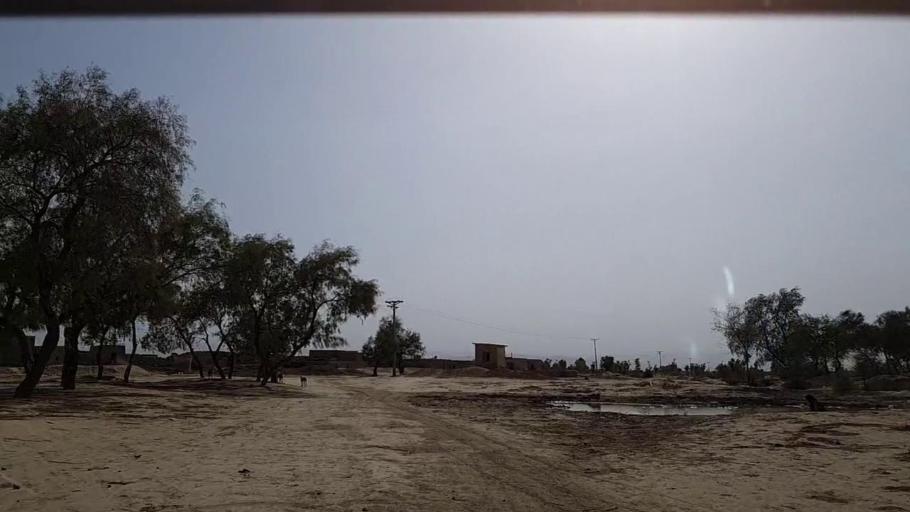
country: PK
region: Sindh
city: Johi
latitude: 26.6060
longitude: 67.4911
